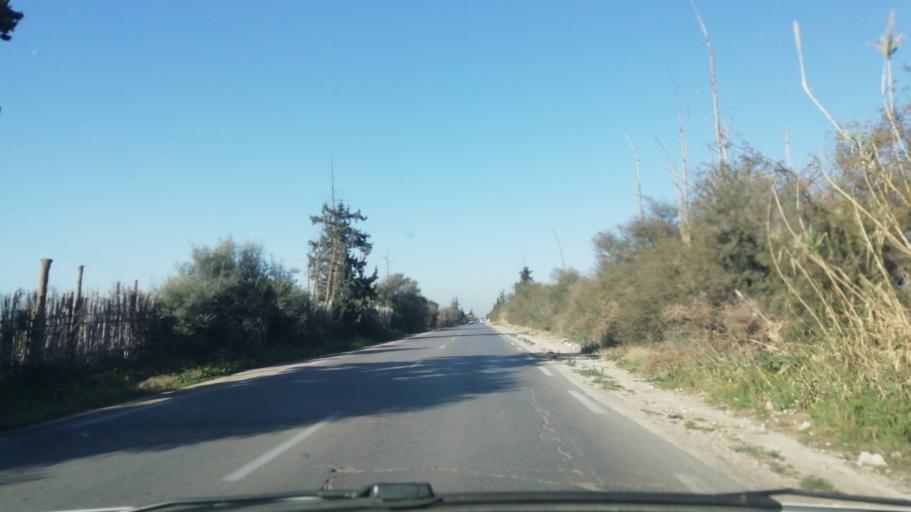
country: DZ
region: Mascara
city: Sig
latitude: 35.5712
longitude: -0.0333
